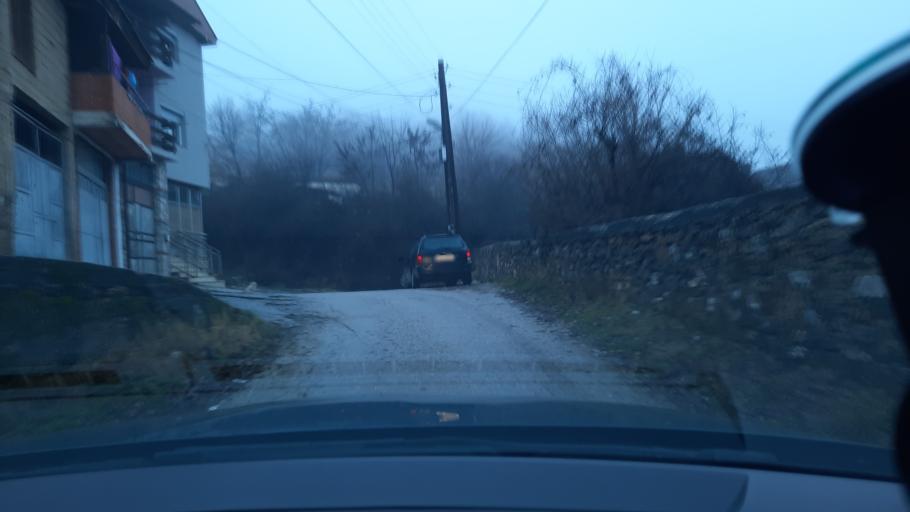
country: MK
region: Vrapciste
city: Vrapciste
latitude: 41.8379
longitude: 20.8820
